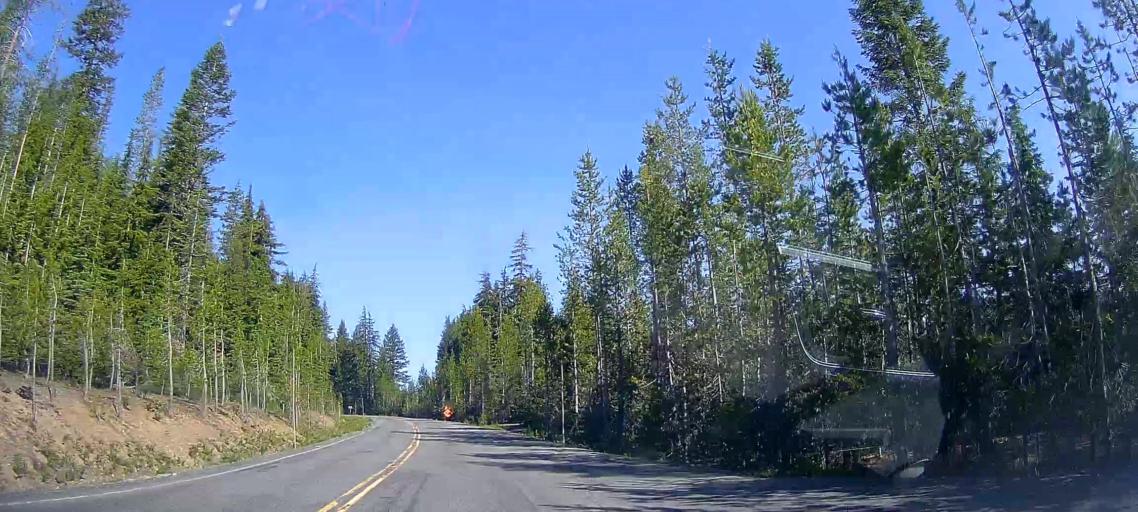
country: US
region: Oregon
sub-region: Jackson County
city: Shady Cove
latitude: 42.8590
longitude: -122.1548
